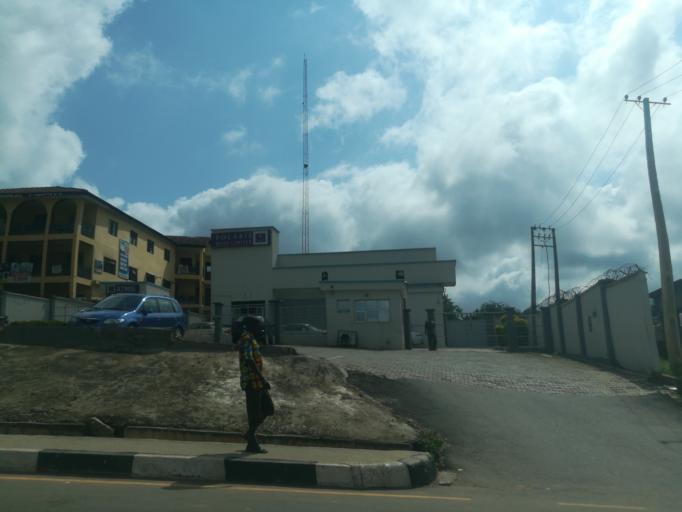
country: NG
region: Oyo
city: Ibadan
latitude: 7.3372
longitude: 3.8704
